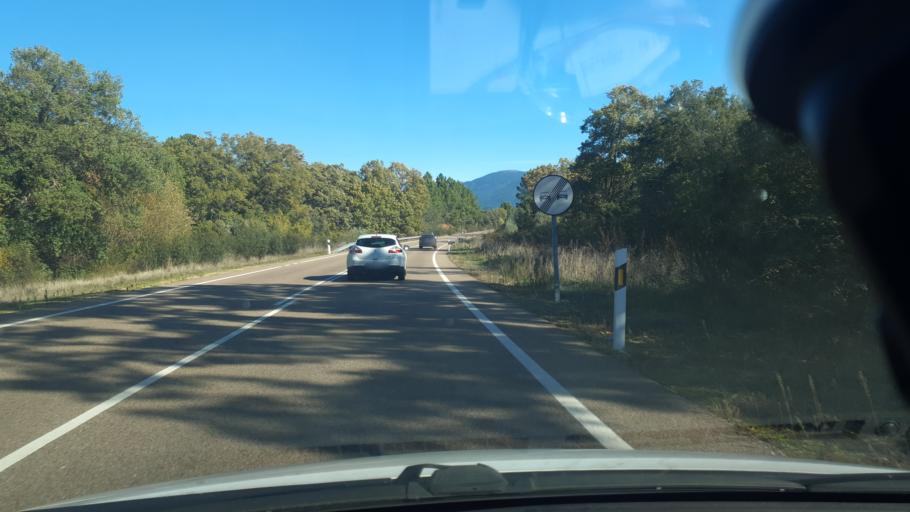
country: ES
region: Castille and Leon
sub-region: Provincia de Avila
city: Arenas de San Pedro
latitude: 40.1691
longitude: -5.1015
